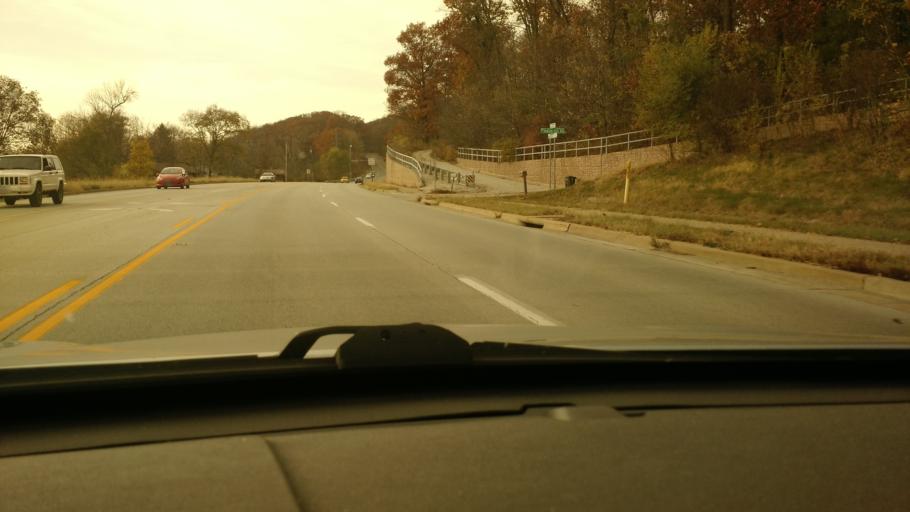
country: US
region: Illinois
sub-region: Rock Island County
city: Milan
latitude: 41.4645
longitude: -90.5622
